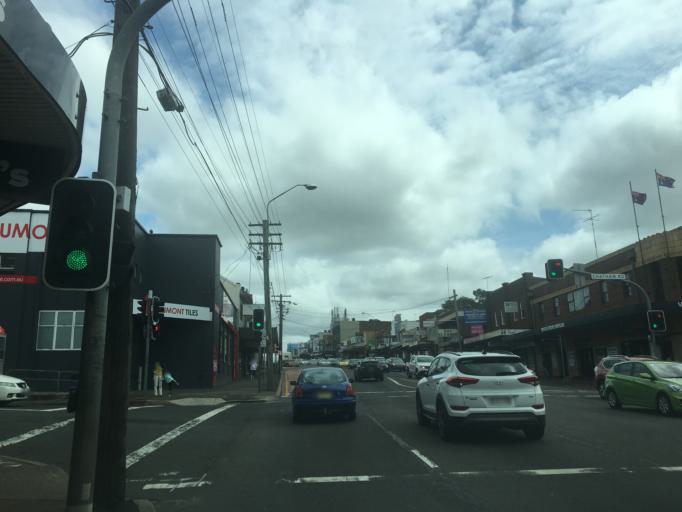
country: AU
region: New South Wales
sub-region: Ryde
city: Denistone
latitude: -33.8076
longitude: 151.0872
